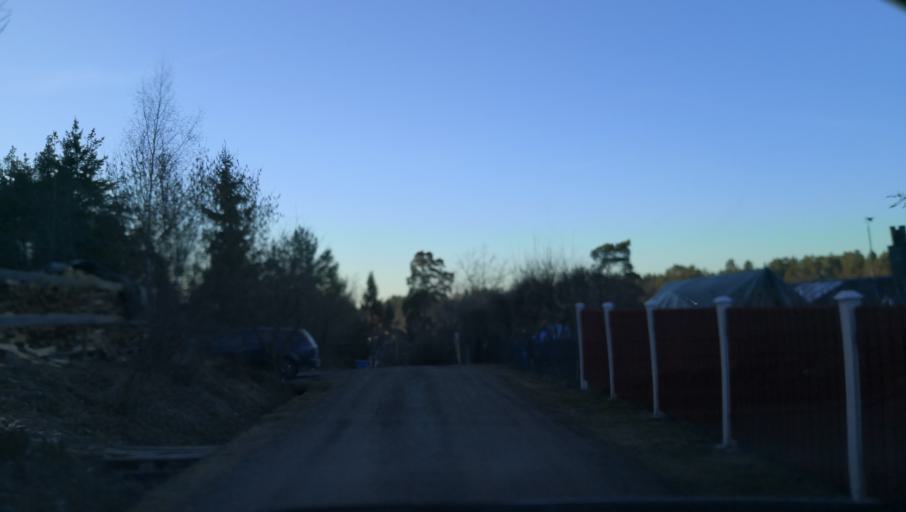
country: SE
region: Stockholm
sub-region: Varmdo Kommun
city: Mortnas
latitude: 59.3360
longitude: 18.4484
